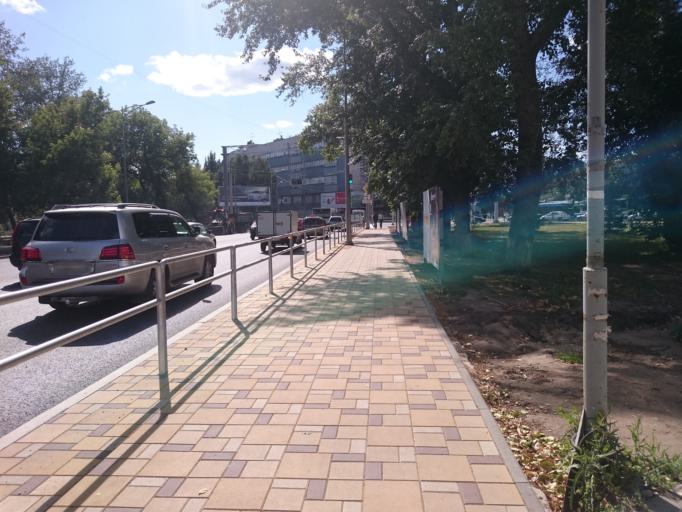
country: RU
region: Samara
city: Samara
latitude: 53.2032
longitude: 50.1404
